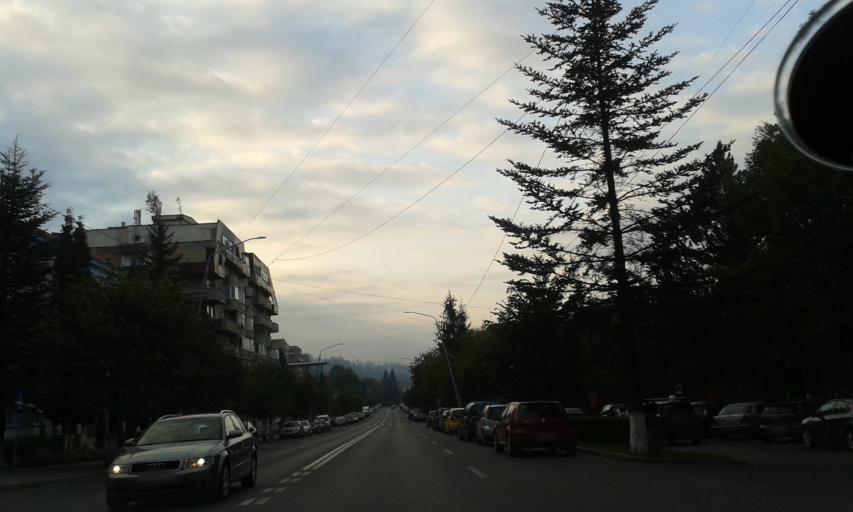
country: RO
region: Hunedoara
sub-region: Municipiul Petrosani
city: Petrosani
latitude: 45.4149
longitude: 23.3739
